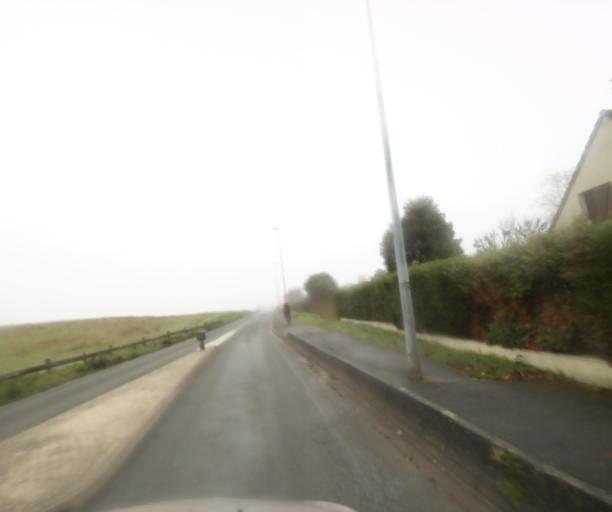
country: FR
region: Ile-de-France
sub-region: Departement de Seine-Saint-Denis
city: Coubron
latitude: 48.9159
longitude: 2.5867
